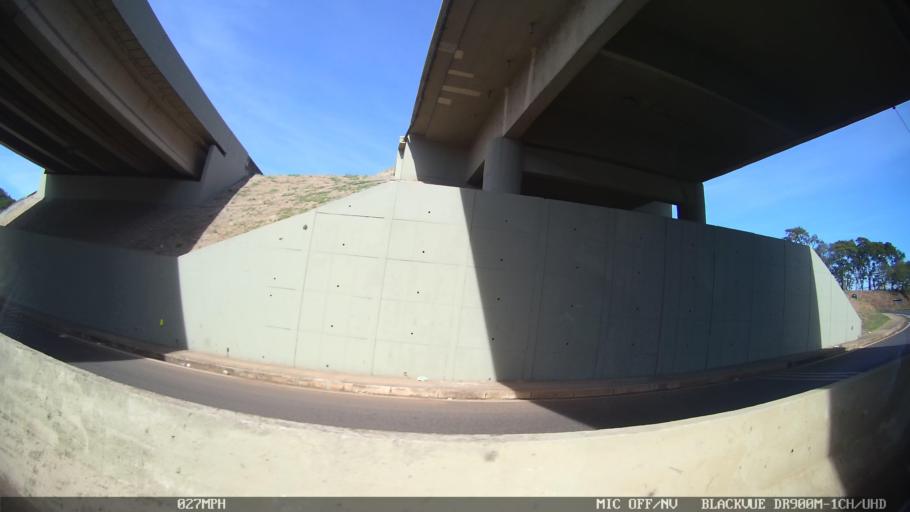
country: BR
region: Sao Paulo
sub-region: Porto Ferreira
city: Porto Ferreira
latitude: -21.8507
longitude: -47.4953
